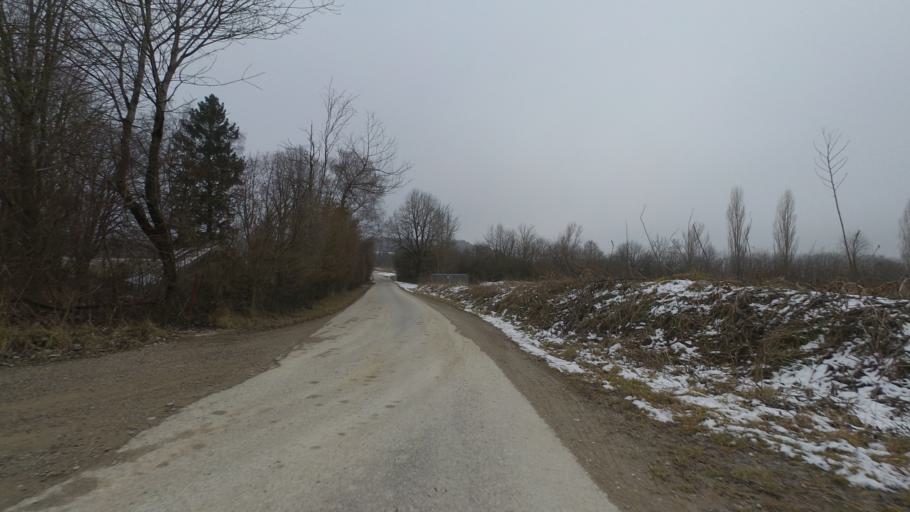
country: DE
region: Bavaria
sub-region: Upper Bavaria
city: Chieming
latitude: 47.8998
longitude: 12.5651
